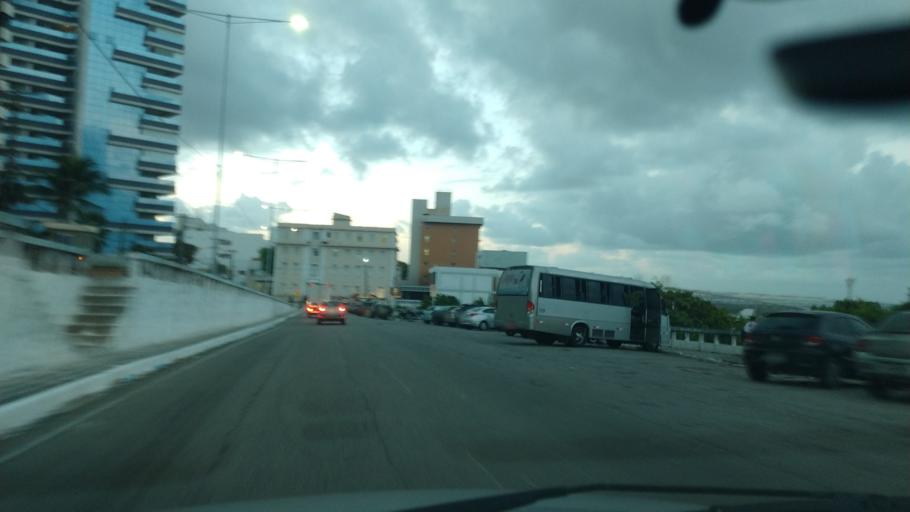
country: BR
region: Rio Grande do Norte
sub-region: Natal
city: Natal
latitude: -5.7817
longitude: -35.1953
